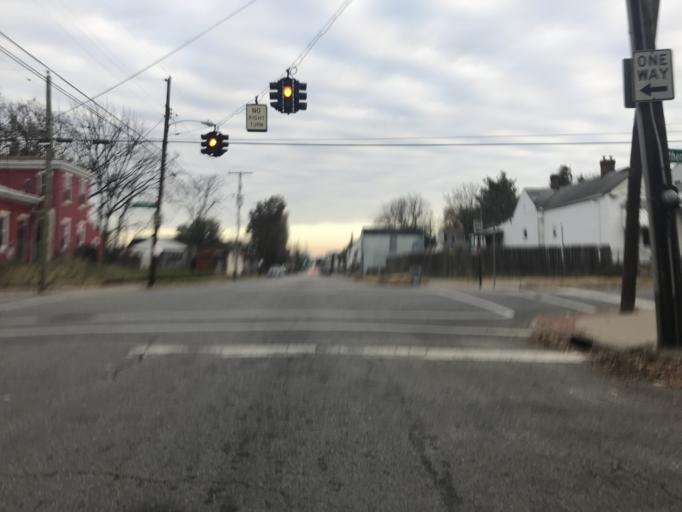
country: US
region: Kentucky
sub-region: Jefferson County
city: Louisville
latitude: 38.2347
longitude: -85.7433
